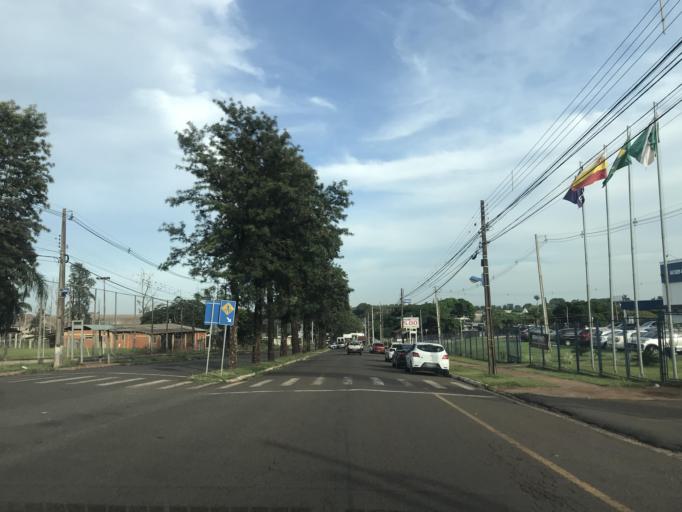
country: BR
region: Parana
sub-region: Maringa
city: Maringa
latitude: -23.4241
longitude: -51.9710
